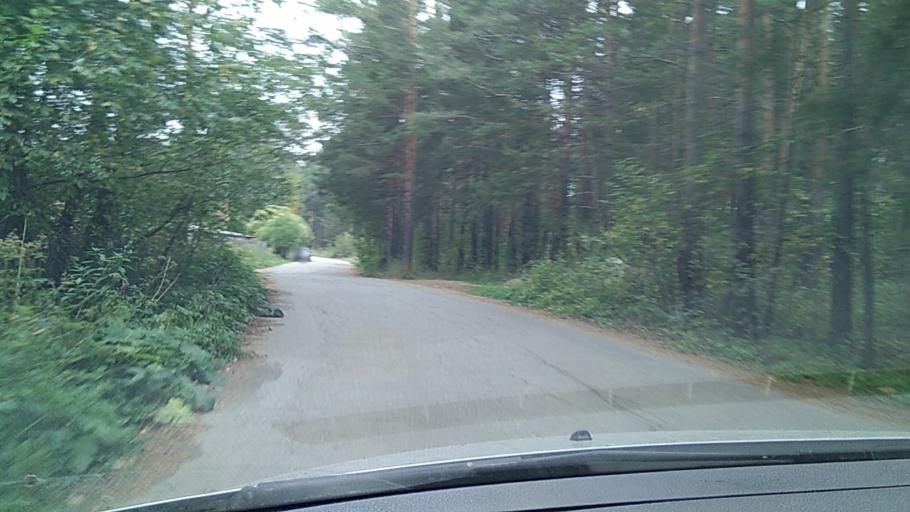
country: RU
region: Chelyabinsk
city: Zlatoust
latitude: 55.1585
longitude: 59.7007
